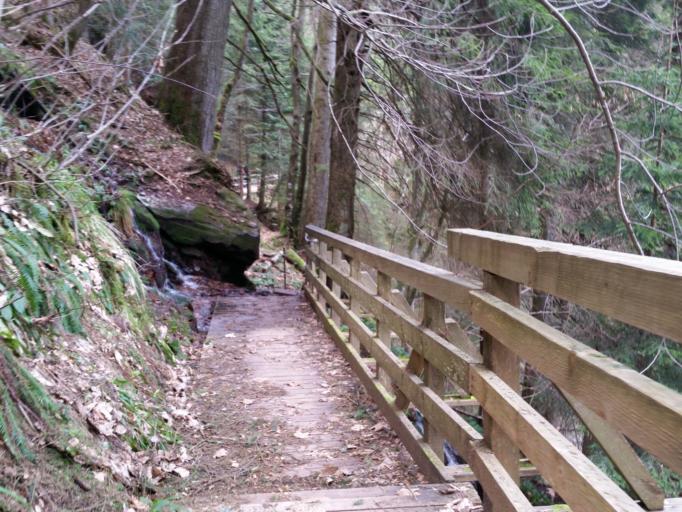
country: DE
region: Baden-Wuerttemberg
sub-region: Karlsruhe Region
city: Baiersbronn
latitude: 48.4848
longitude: 8.3333
